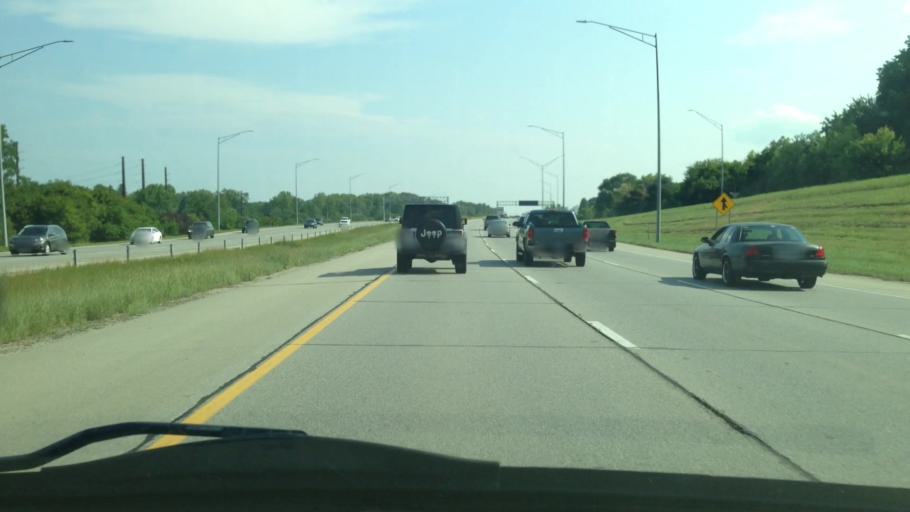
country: US
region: Iowa
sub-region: Linn County
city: Cedar Rapids
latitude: 42.0110
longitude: -91.6666
